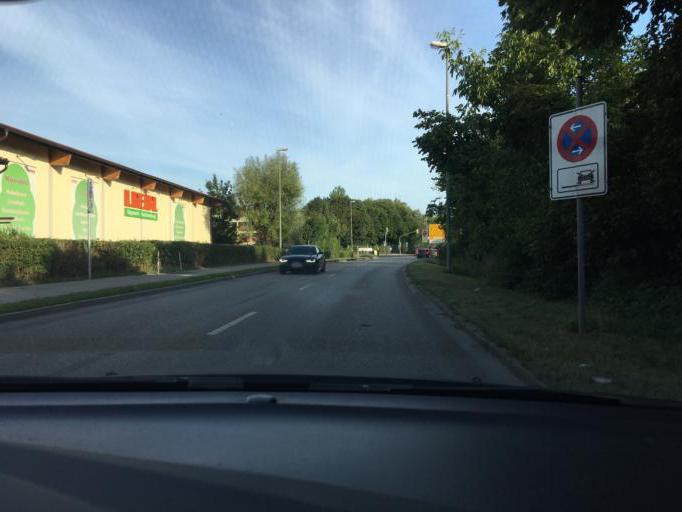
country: DE
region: Bavaria
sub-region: Upper Bavaria
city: Erding
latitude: 48.3110
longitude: 11.9166
